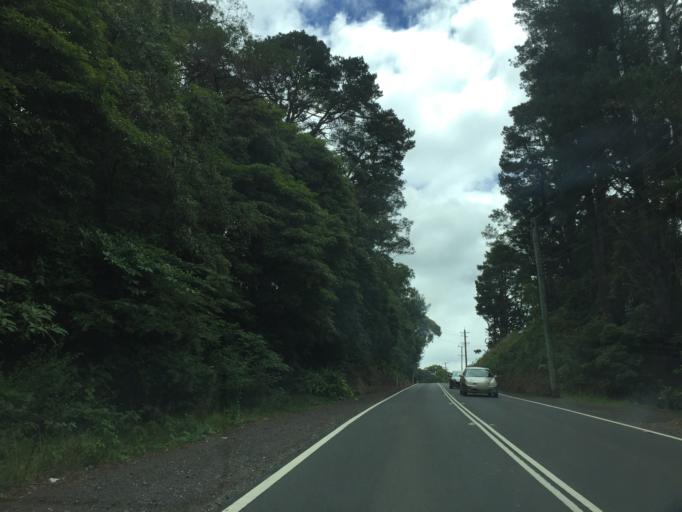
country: AU
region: New South Wales
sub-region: Hawkesbury
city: Richmond
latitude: -33.5220
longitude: 150.6279
